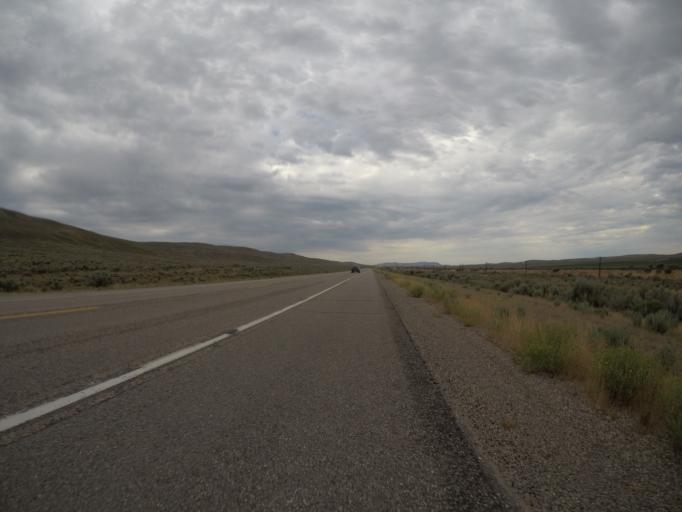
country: US
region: Utah
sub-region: Rich County
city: Randolph
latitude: 41.8473
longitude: -110.9739
